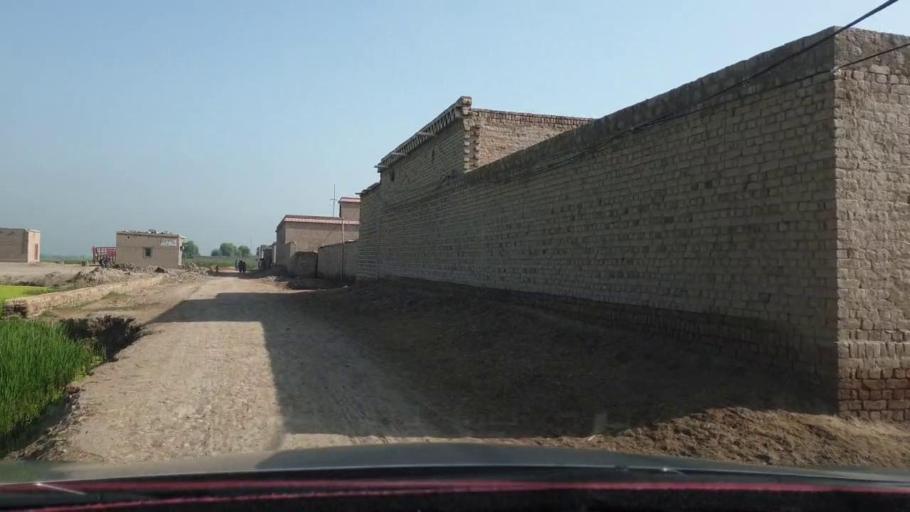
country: PK
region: Sindh
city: Nasirabad
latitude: 27.4757
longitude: 67.9248
